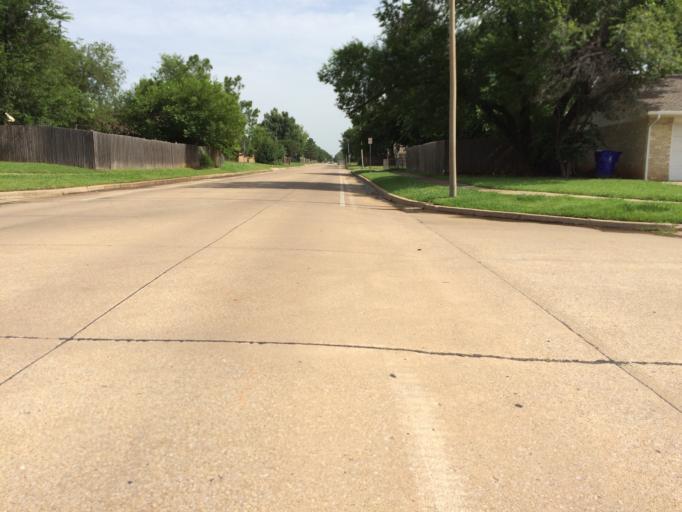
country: US
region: Oklahoma
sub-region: Cleveland County
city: Norman
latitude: 35.2140
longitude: -97.4162
